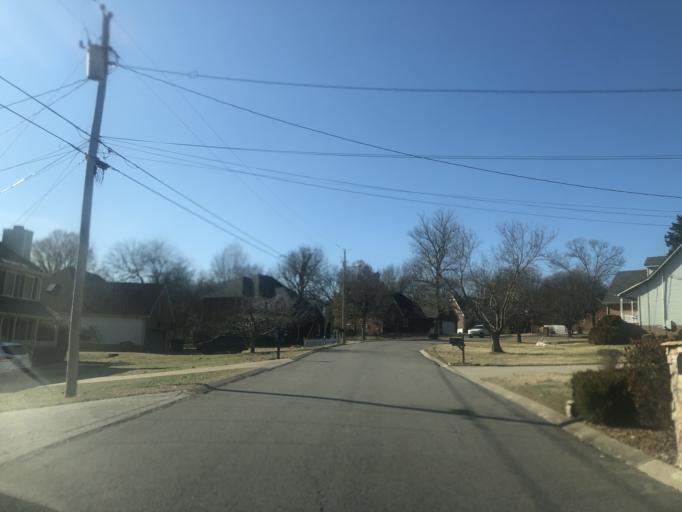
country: US
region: Tennessee
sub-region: Rutherford County
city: Smyrna
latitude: 35.9765
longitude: -86.5400
